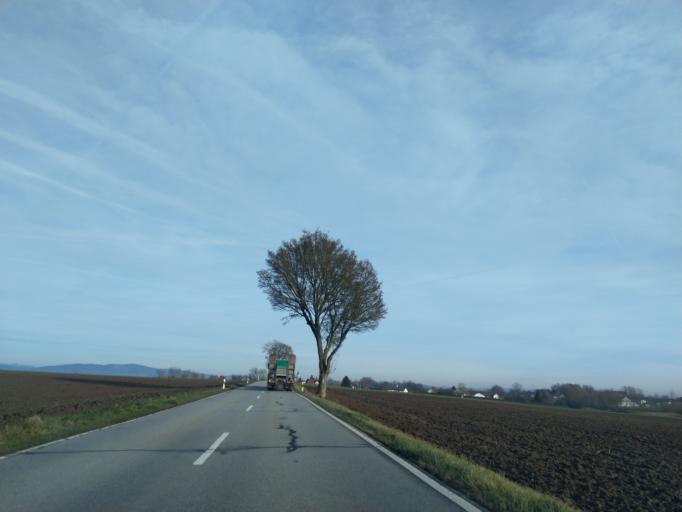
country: DE
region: Bavaria
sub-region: Lower Bavaria
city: Buchhofen
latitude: 48.7007
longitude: 12.9613
